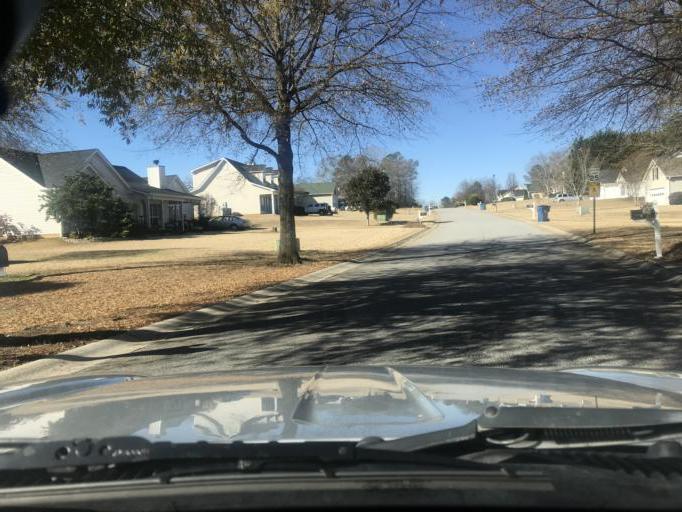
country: US
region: Georgia
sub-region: Barrow County
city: Winder
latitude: 33.9277
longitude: -83.7701
